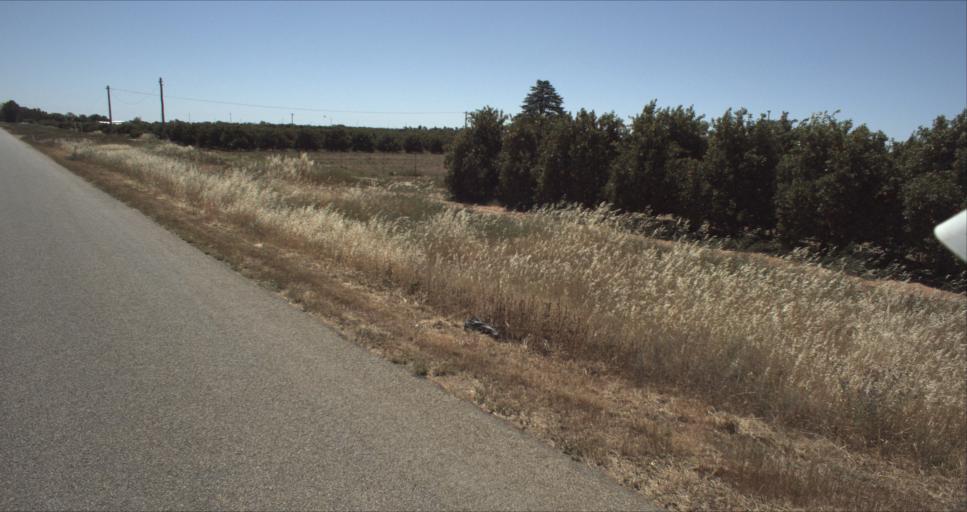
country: AU
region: New South Wales
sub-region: Leeton
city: Leeton
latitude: -34.5430
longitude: 146.3653
